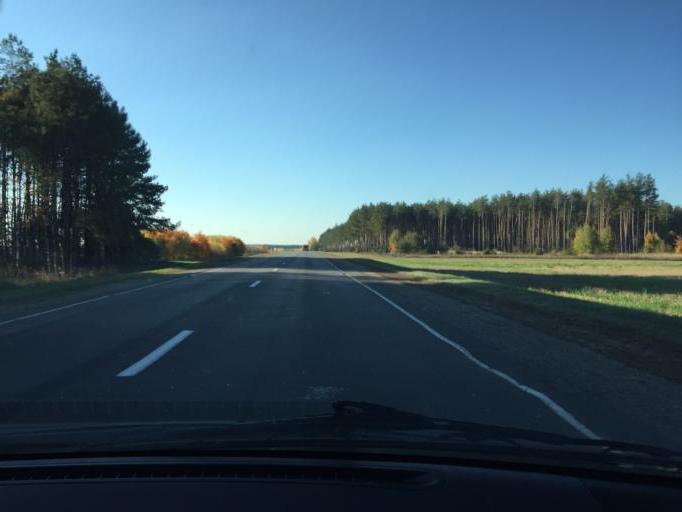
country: BY
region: Brest
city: Luninyets
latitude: 52.2720
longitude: 26.9893
